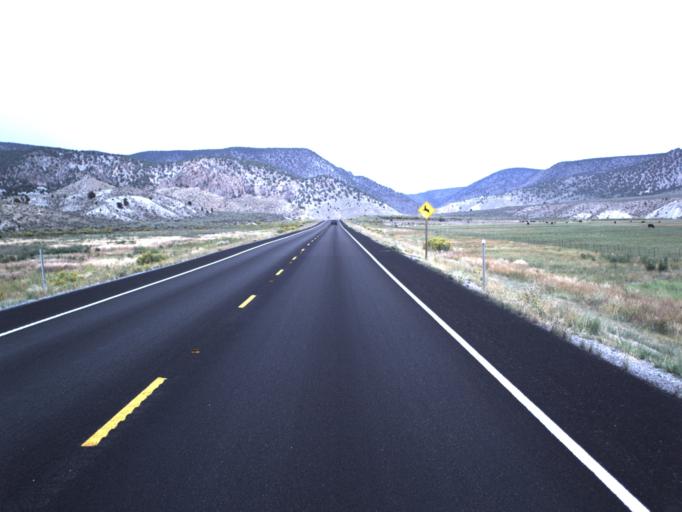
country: US
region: Utah
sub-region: Garfield County
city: Panguitch
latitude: 38.0385
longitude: -112.3555
